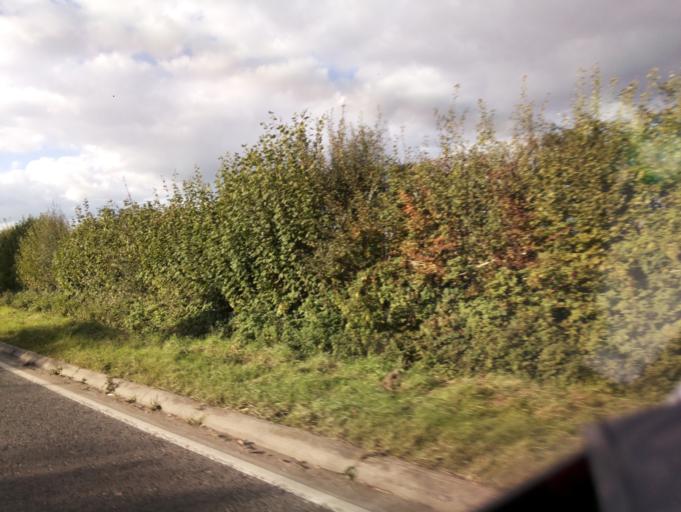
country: GB
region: England
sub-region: Herefordshire
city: Kinnersley
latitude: 52.1187
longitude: -2.9880
